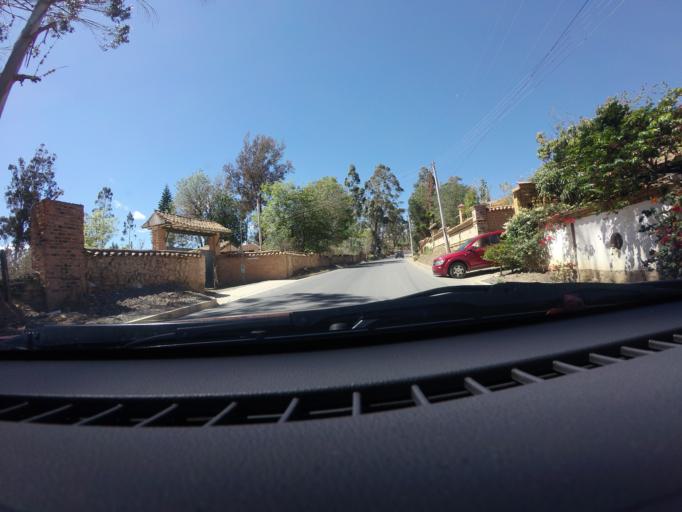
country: CO
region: Boyaca
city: Villa de Leiva
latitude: 5.6291
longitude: -73.5382
